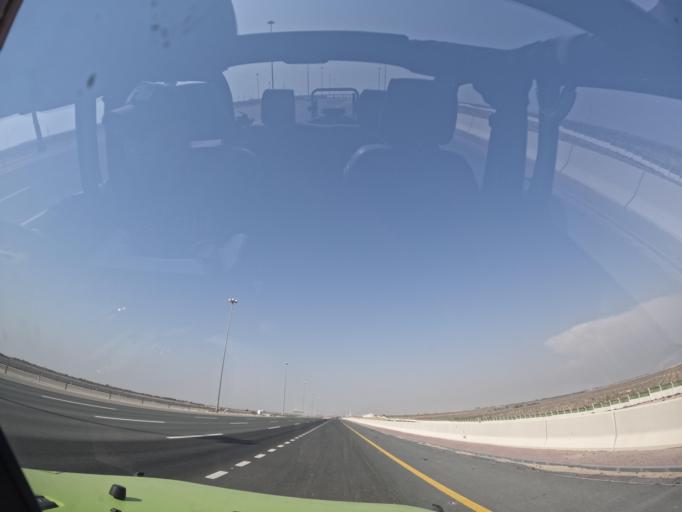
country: AE
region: Abu Dhabi
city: Abu Dhabi
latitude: 24.6222
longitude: 54.7699
